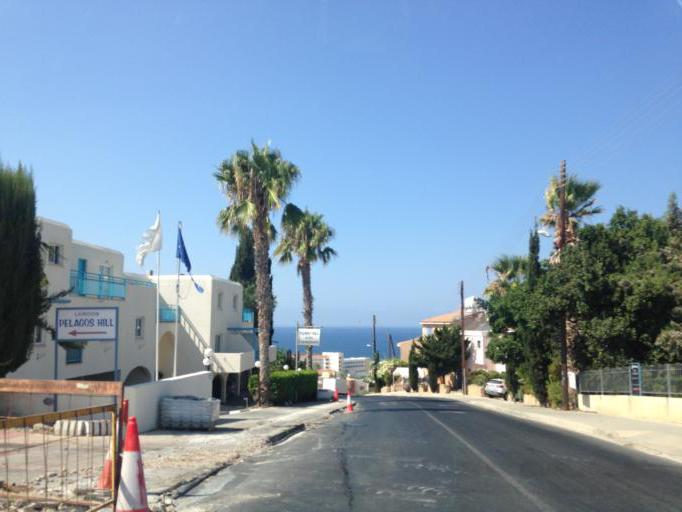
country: CY
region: Pafos
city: Chlorakas
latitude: 34.8043
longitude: 32.4020
